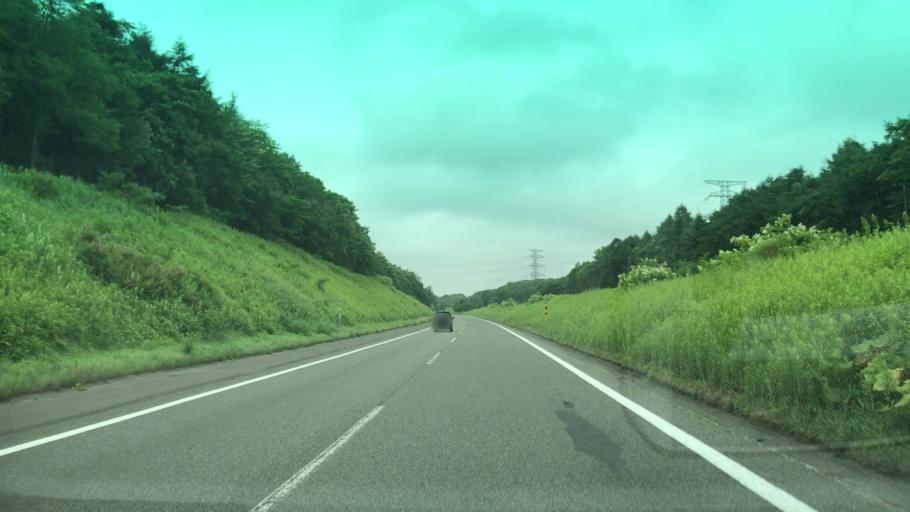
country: JP
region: Hokkaido
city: Chitose
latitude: 42.7324
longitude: 141.6528
